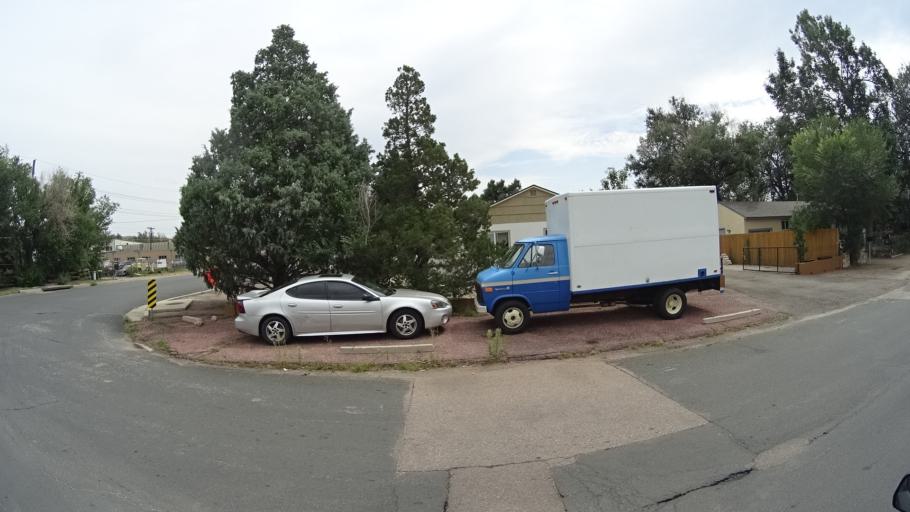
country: US
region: Colorado
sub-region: El Paso County
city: Colorado Springs
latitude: 38.8776
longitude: -104.8270
